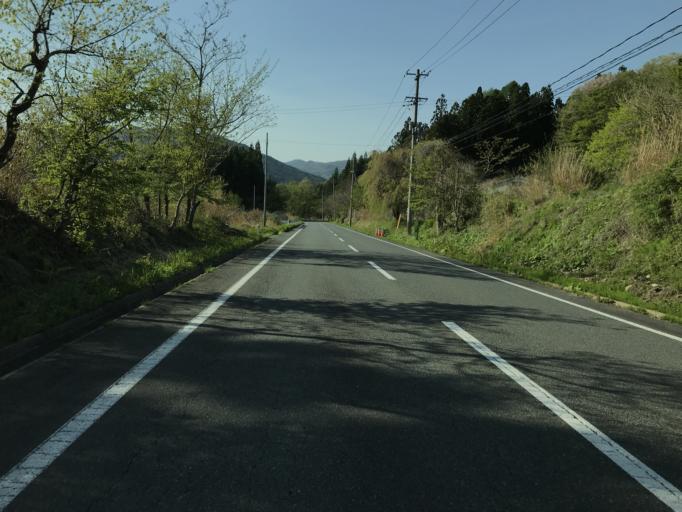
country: JP
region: Fukushima
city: Funehikimachi-funehiki
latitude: 37.5403
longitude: 140.7407
